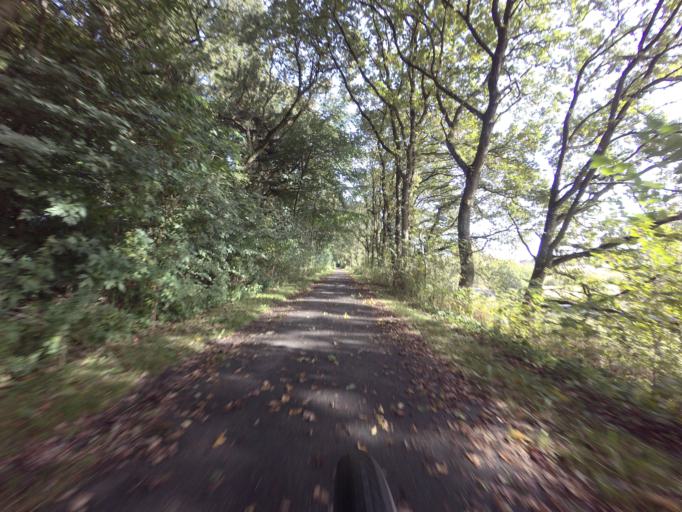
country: DK
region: Central Jutland
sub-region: Viborg Kommune
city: Viborg
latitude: 56.4324
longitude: 9.4614
